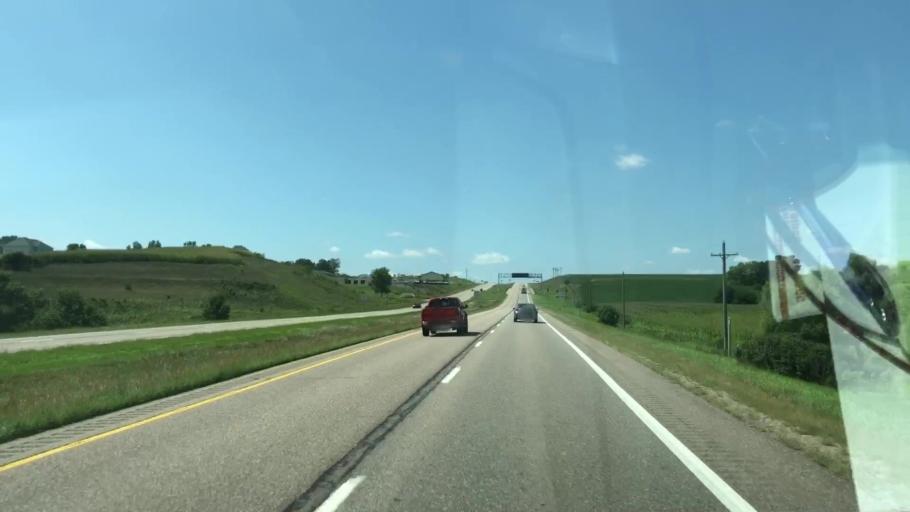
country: US
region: Iowa
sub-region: Woodbury County
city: Sergeant Bluff
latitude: 42.4755
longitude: -96.2884
